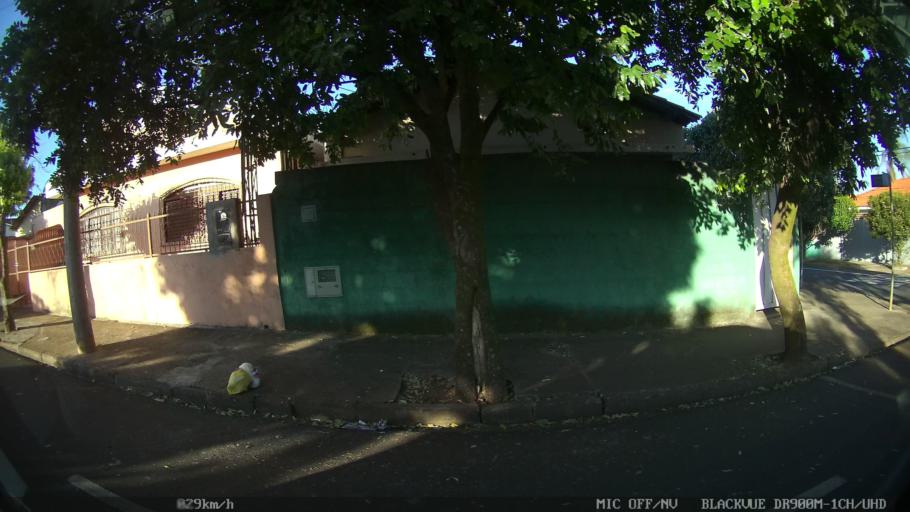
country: BR
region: Sao Paulo
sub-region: Franca
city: Franca
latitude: -20.5297
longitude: -47.3775
